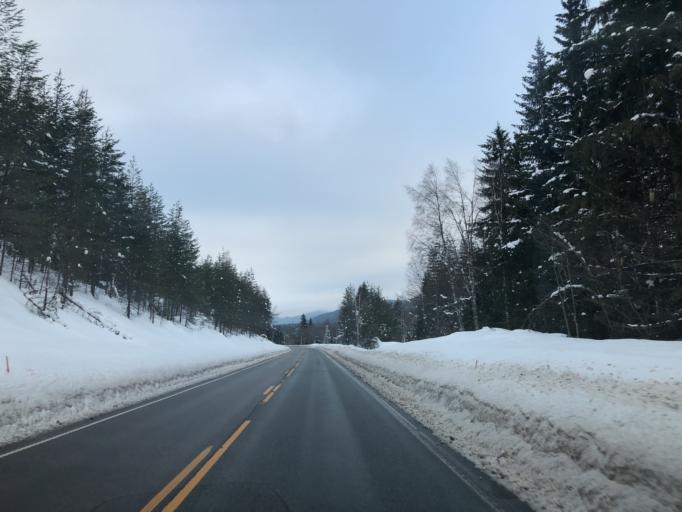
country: NO
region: Hedmark
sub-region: Trysil
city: Innbygda
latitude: 61.2663
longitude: 12.3067
